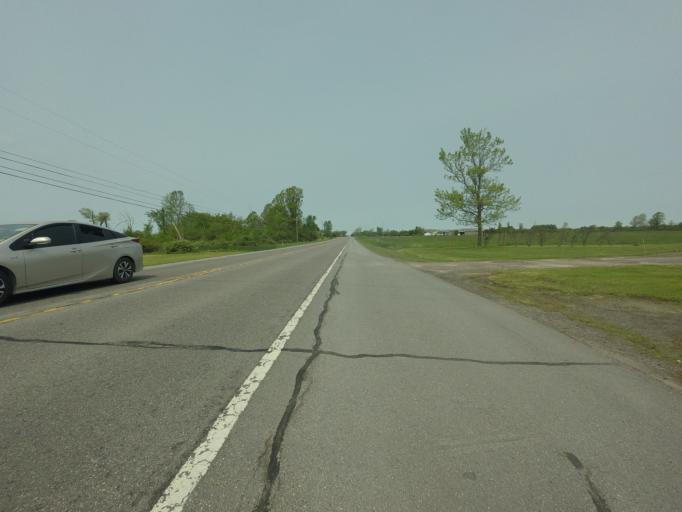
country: US
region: New York
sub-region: Jefferson County
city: Dexter
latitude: 44.0323
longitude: -76.0558
